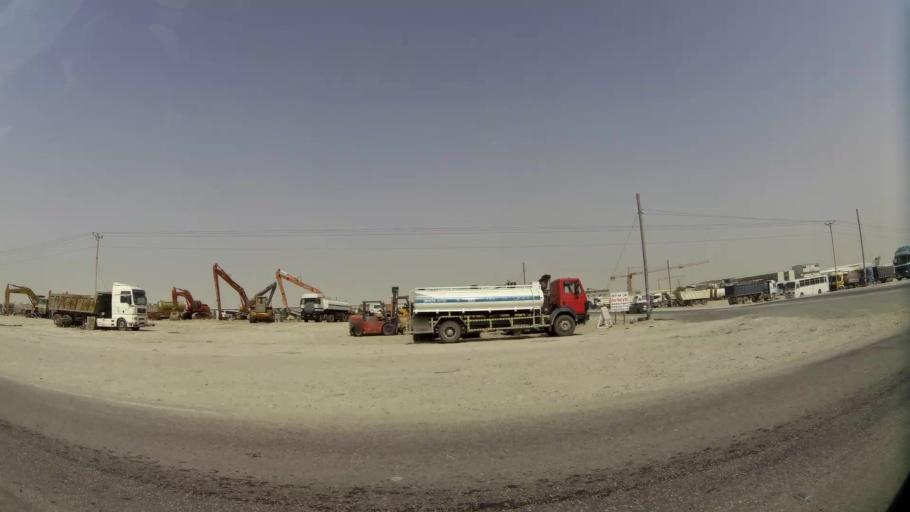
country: QA
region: Baladiyat ar Rayyan
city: Ar Rayyan
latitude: 25.2030
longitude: 51.3642
